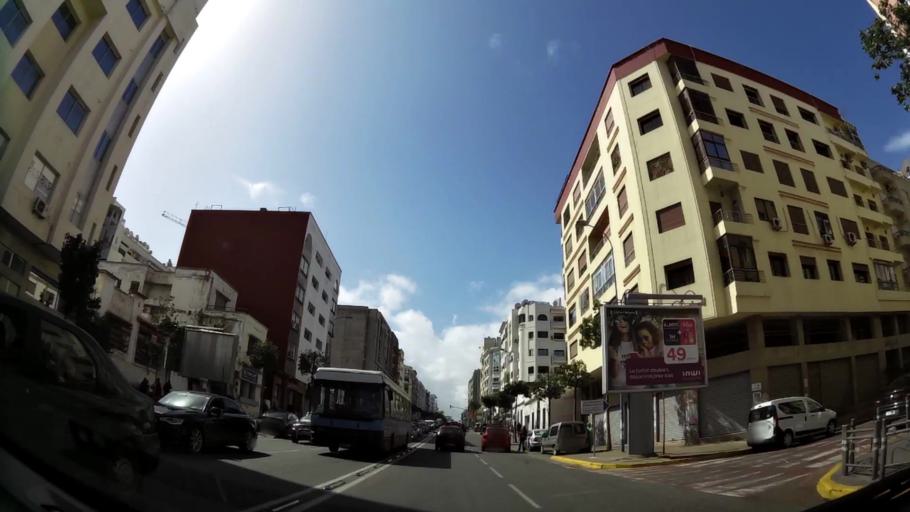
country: MA
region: Grand Casablanca
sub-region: Casablanca
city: Casablanca
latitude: 33.5820
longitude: -7.6151
